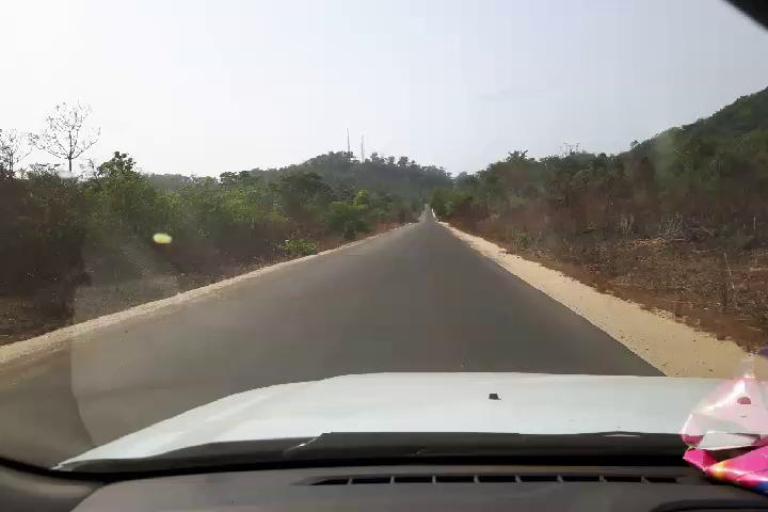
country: SL
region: Western Area
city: Waterloo
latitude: 8.2584
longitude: -13.1597
